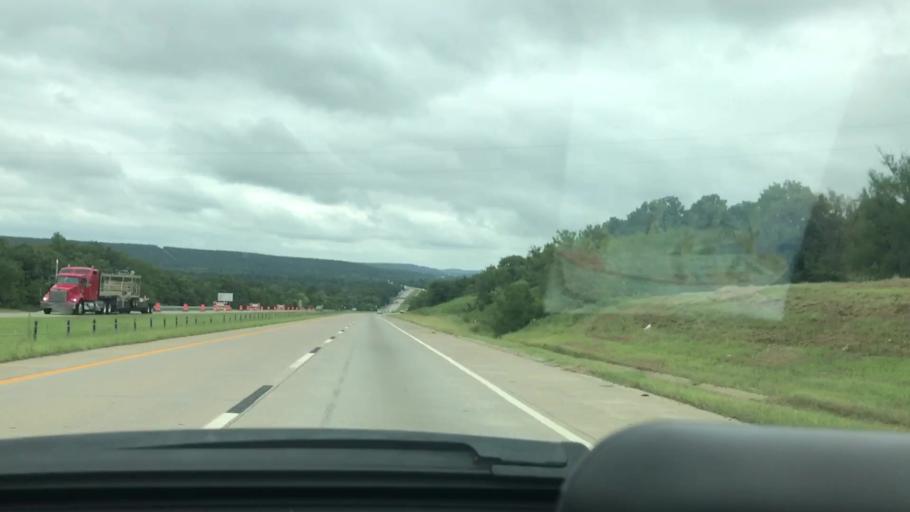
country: US
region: Oklahoma
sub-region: Pittsburg County
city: Krebs
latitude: 34.9907
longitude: -95.7216
